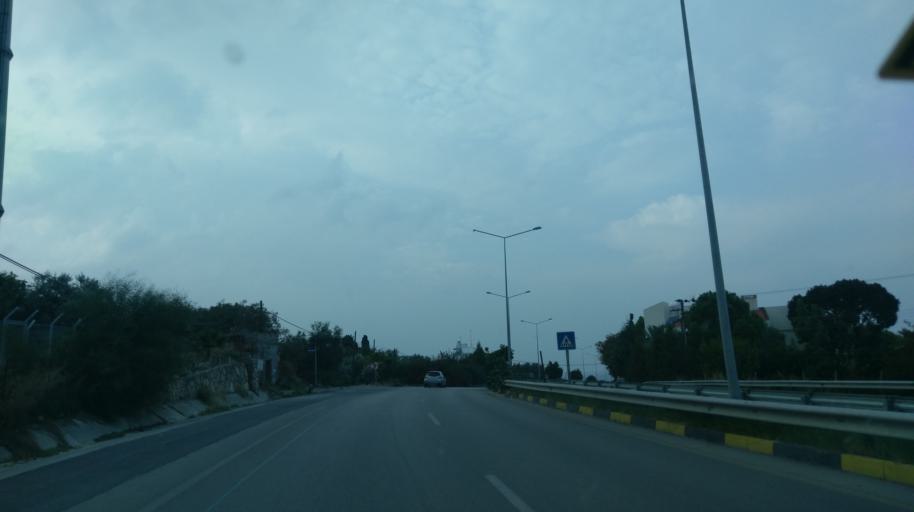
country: CY
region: Keryneia
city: Kyrenia
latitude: 35.3363
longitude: 33.2584
